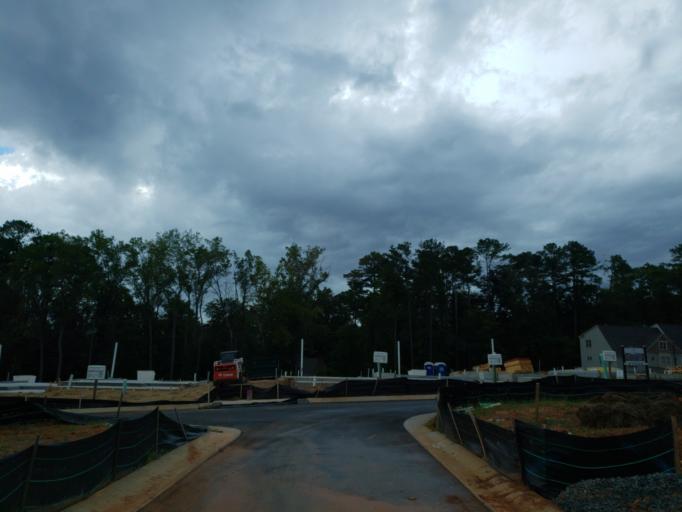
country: US
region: Georgia
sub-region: Cherokee County
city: Woodstock
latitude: 34.0926
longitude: -84.5237
